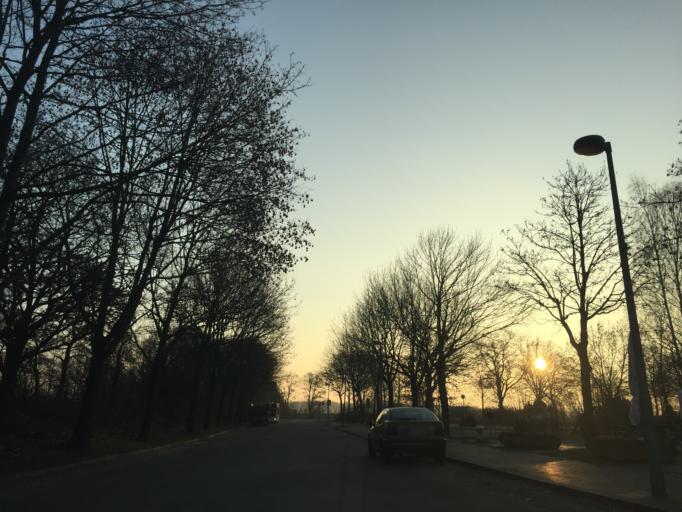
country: DE
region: Berlin
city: Gatow
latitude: 52.4971
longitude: 13.1554
